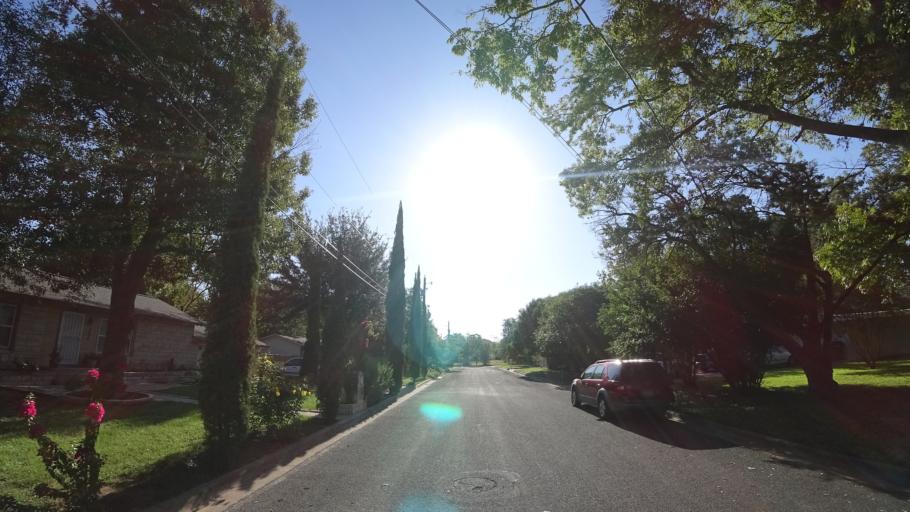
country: US
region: Texas
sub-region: Travis County
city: Austin
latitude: 30.3513
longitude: -97.6988
